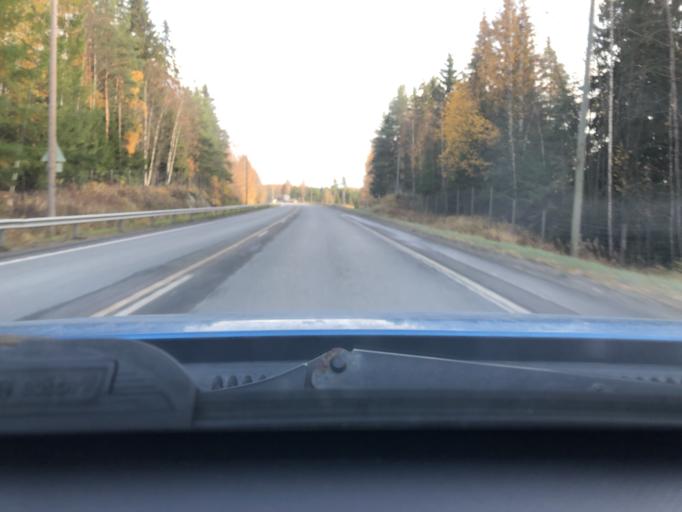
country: FI
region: Pirkanmaa
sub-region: Tampere
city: Kangasala
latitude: 61.4678
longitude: 23.9926
